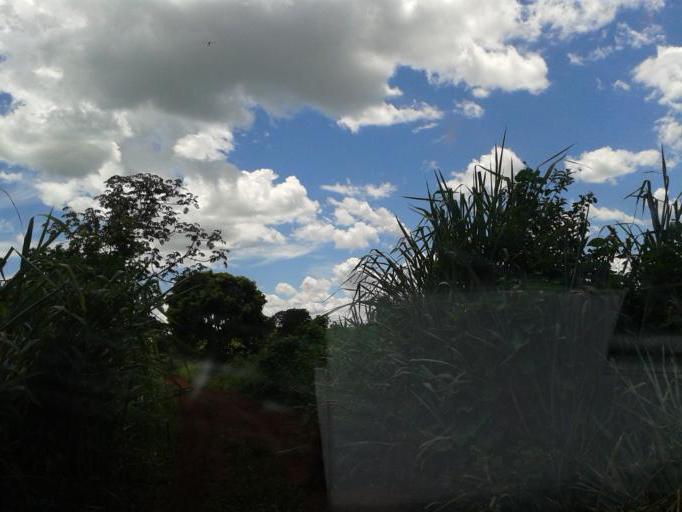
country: BR
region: Minas Gerais
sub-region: Santa Vitoria
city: Santa Vitoria
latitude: -18.6957
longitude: -50.1996
